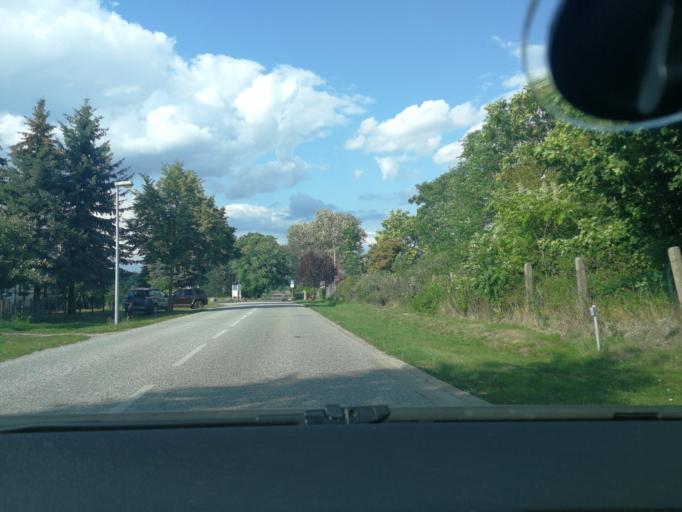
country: DE
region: Brandenburg
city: Pritzwalk
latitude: 53.1601
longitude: 12.1818
